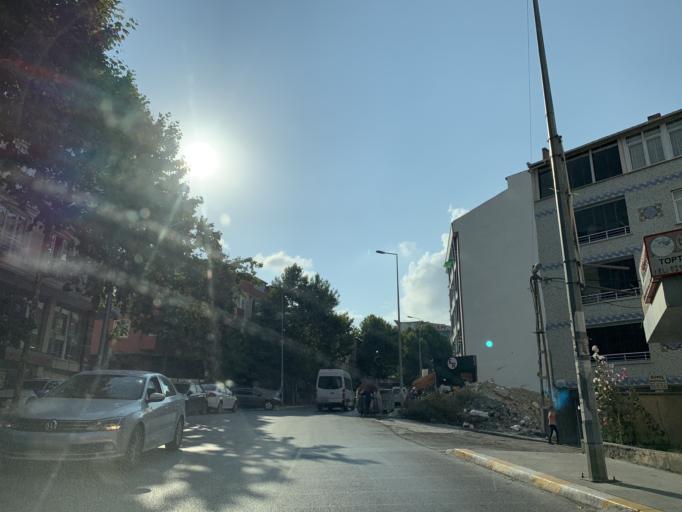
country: TR
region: Istanbul
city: Esenyurt
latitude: 41.0439
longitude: 28.6884
